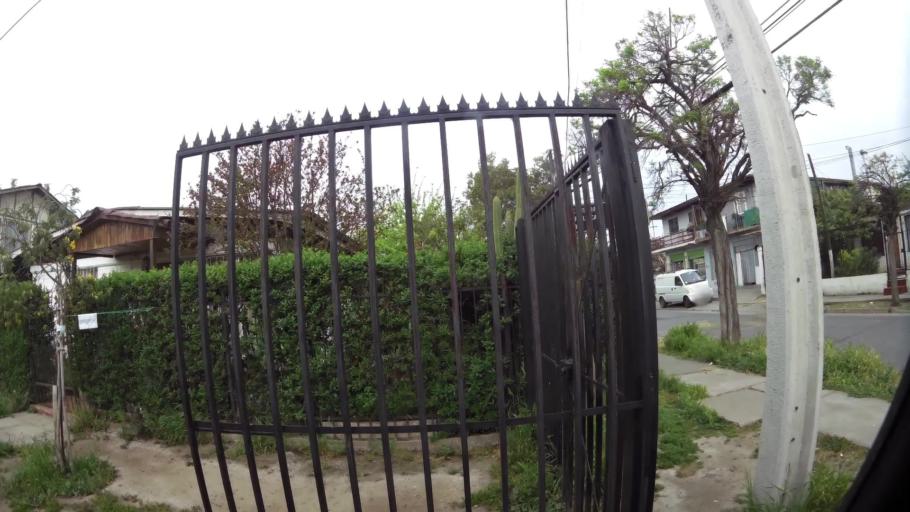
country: CL
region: Santiago Metropolitan
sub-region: Provincia de Santiago
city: Lo Prado
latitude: -33.5151
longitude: -70.7714
